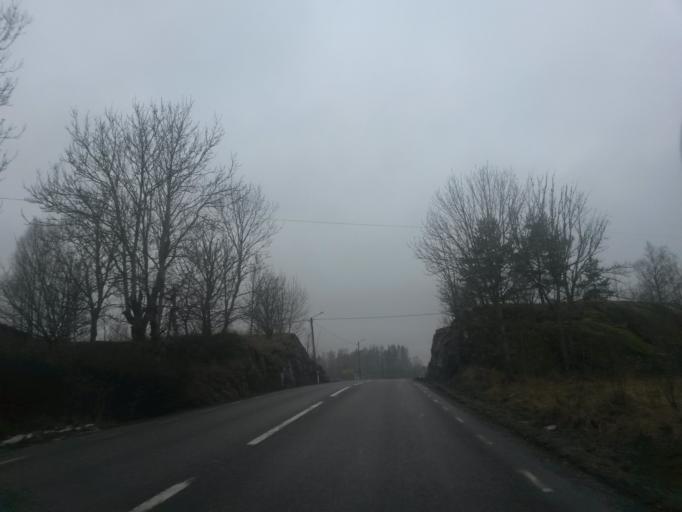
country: SE
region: Vaestra Goetaland
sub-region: Vanersborgs Kommun
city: Vargon
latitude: 58.2562
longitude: 12.4069
